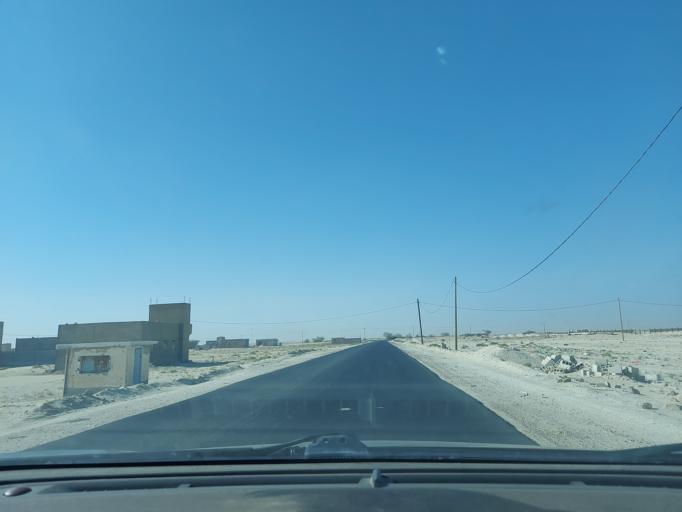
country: MR
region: Nouakchott
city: Nouakchott
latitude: 17.9953
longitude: -15.9882
